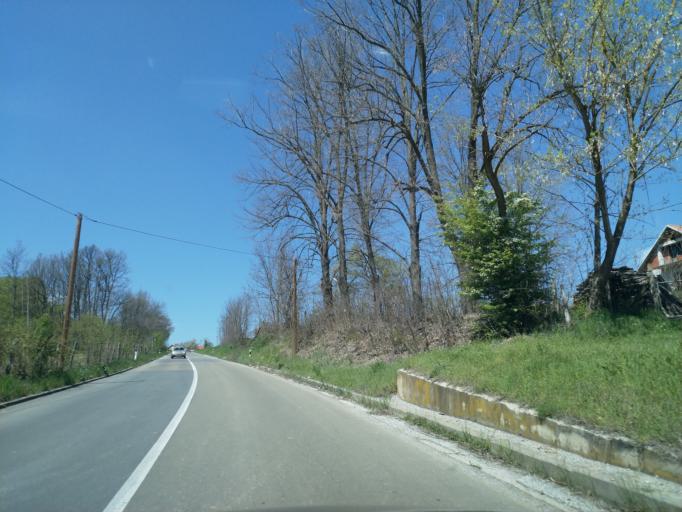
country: RS
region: Central Serbia
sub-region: Belgrade
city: Lazarevac
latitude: 44.3613
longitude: 20.3514
